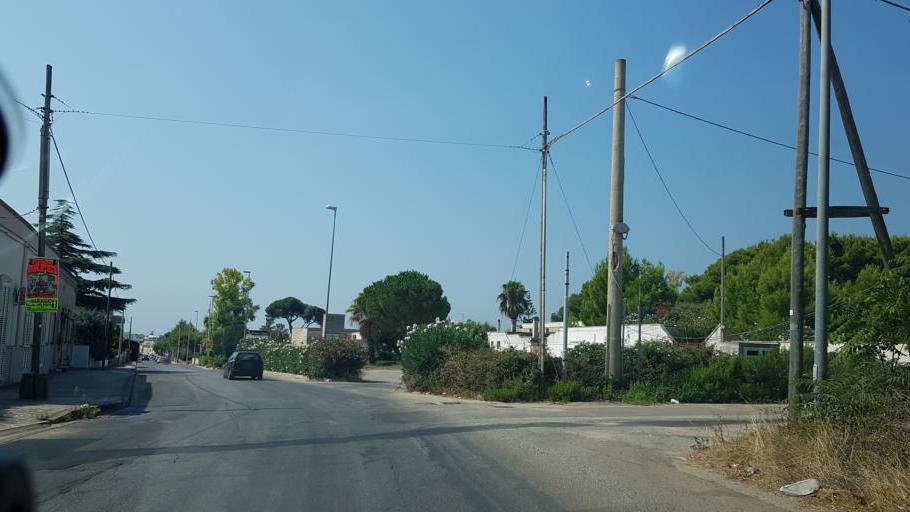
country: IT
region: Apulia
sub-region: Provincia di Taranto
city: Maruggio
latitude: 40.3295
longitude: 17.5744
